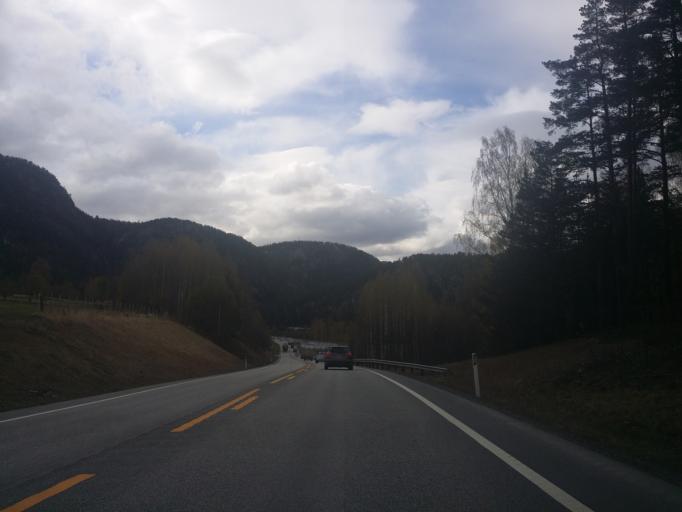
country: NO
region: Buskerud
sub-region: Nes
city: Nesbyen
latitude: 60.4676
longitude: 9.2458
